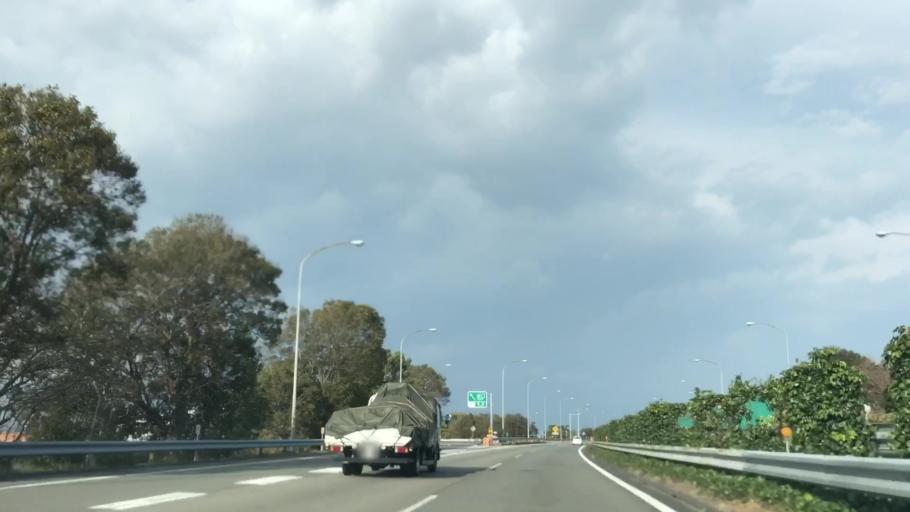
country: JP
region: Shizuoka
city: Shimada
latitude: 34.7894
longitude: 138.2324
